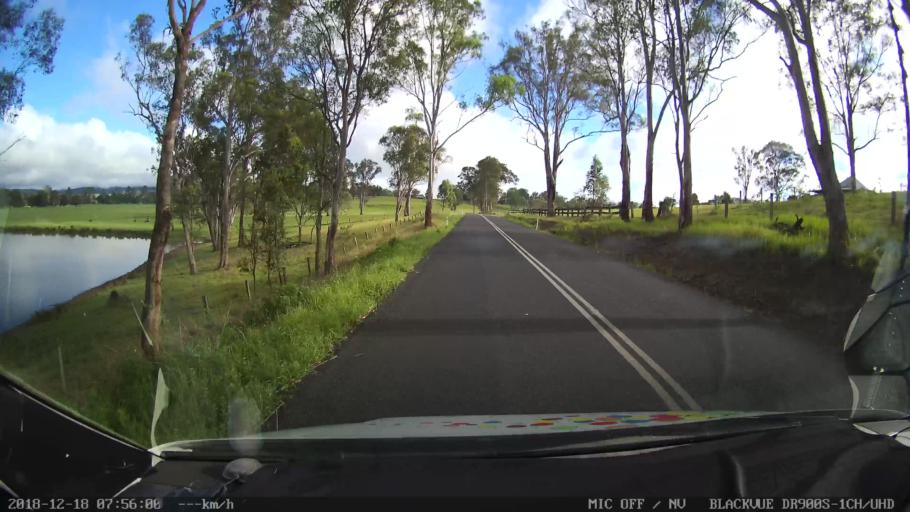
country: AU
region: New South Wales
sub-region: Kyogle
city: Kyogle
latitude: -28.4030
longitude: 152.6035
